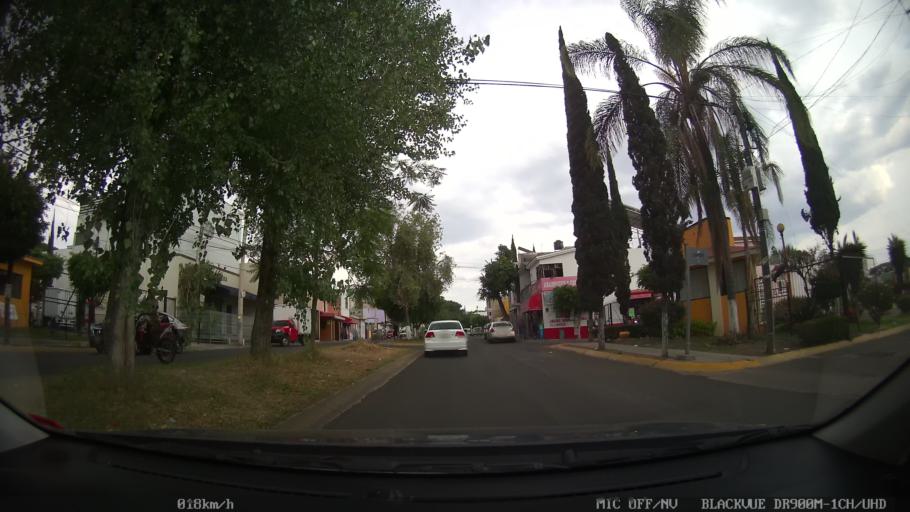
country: MX
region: Jalisco
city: Tlaquepaque
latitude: 20.6273
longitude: -103.2802
